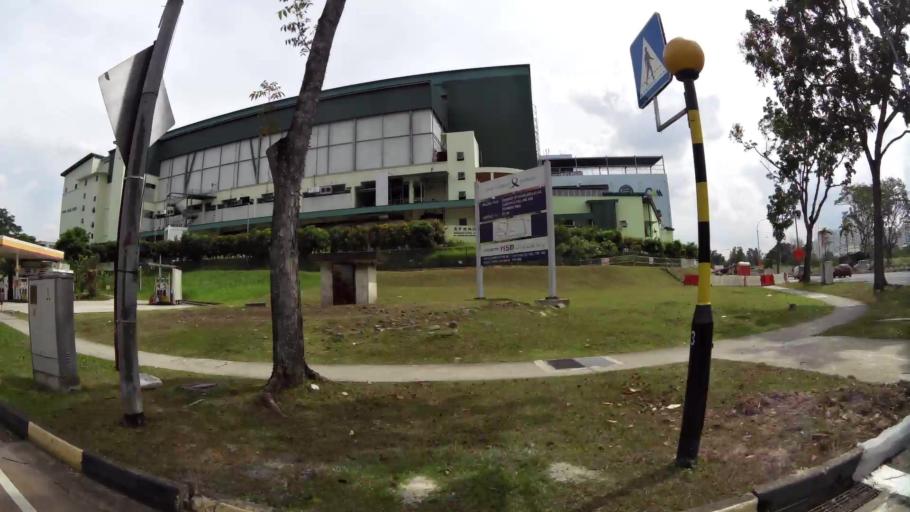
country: MY
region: Johor
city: Johor Bahru
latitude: 1.4114
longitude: 103.7560
